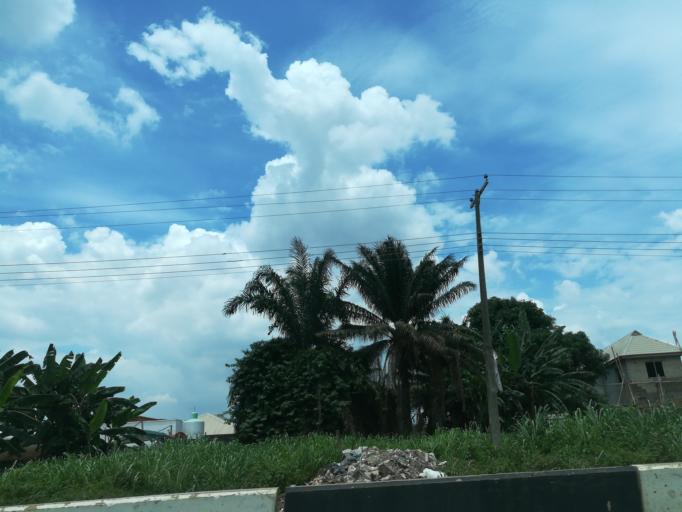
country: NG
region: Lagos
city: Ebute Ikorodu
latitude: 6.5989
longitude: 3.4994
